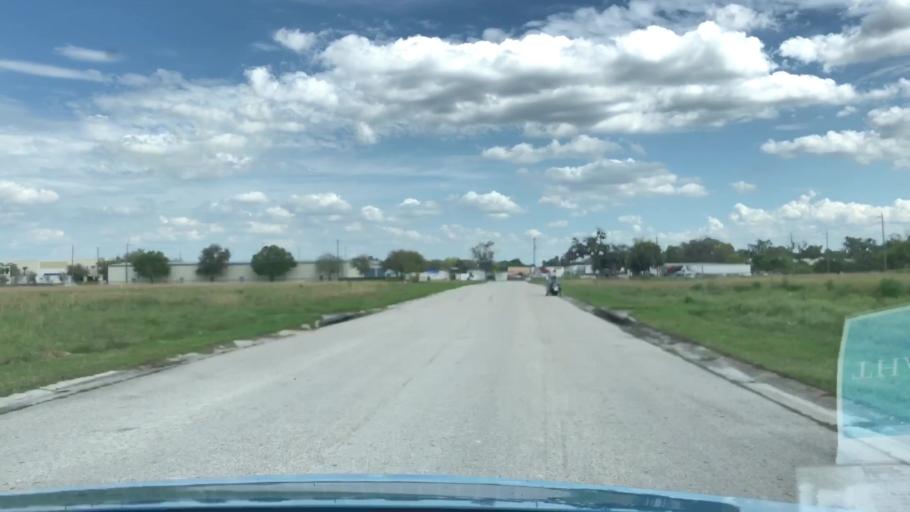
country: US
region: Florida
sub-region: Seminole County
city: Sanford
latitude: 28.8217
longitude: -81.3291
